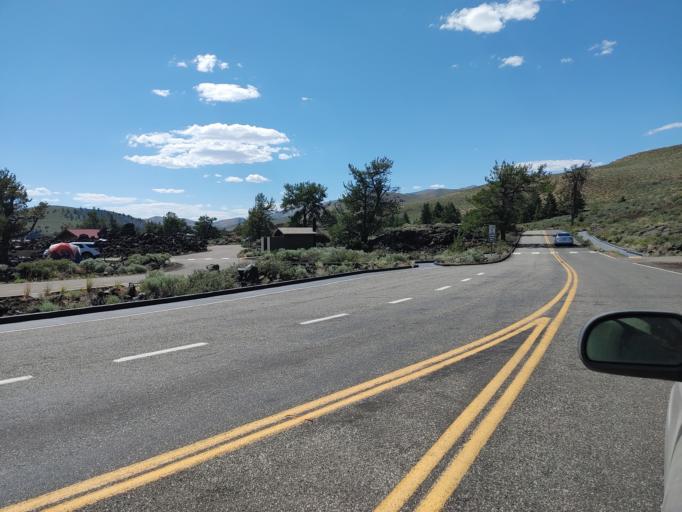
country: US
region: Idaho
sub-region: Butte County
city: Arco
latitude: 43.4612
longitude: -113.5568
